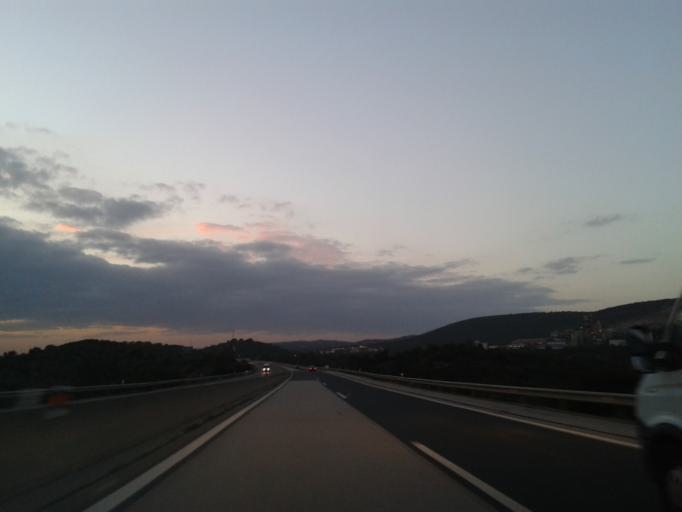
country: PT
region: Faro
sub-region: Loule
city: Vilamoura
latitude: 37.1271
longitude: -8.0913
